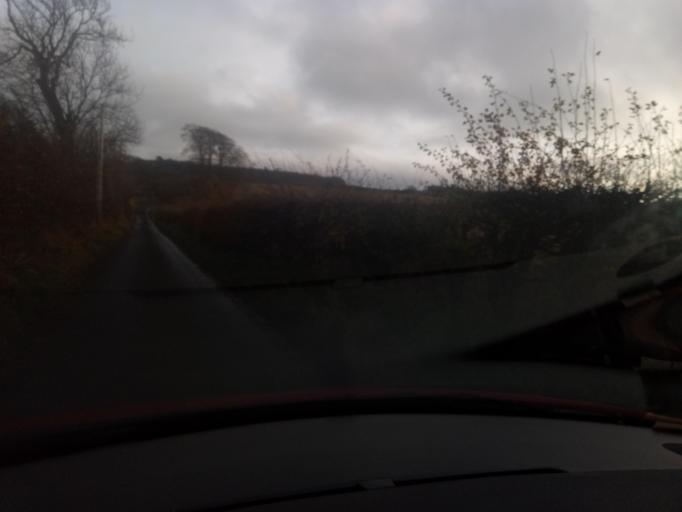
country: GB
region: Scotland
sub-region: The Scottish Borders
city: Jedburgh
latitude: 55.4876
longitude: -2.6145
